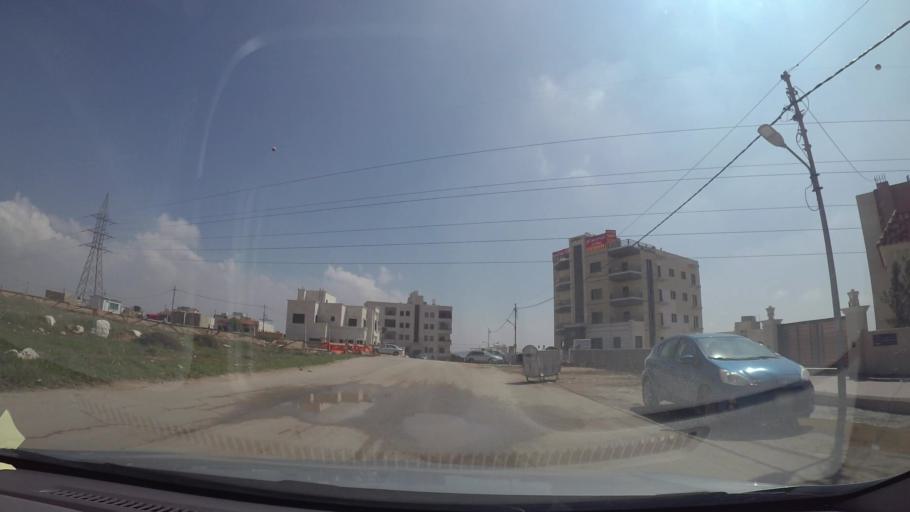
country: JO
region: Amman
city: Al Bunayyat ash Shamaliyah
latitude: 31.8883
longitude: 35.8958
